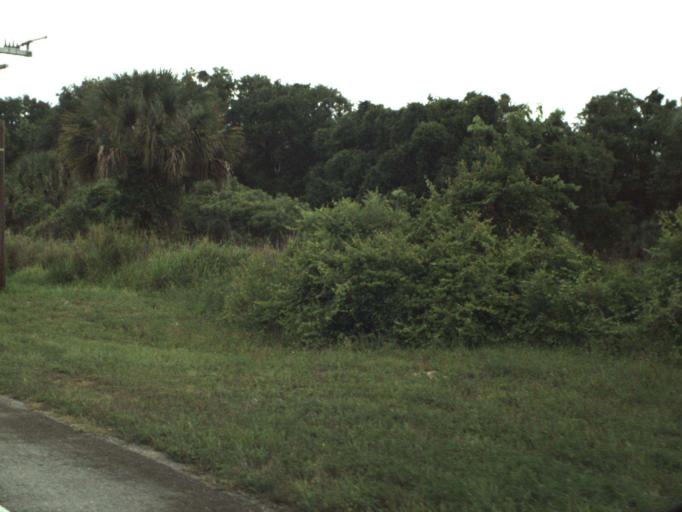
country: US
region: Florida
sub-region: Brevard County
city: Mims
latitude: 28.6654
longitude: -80.9280
